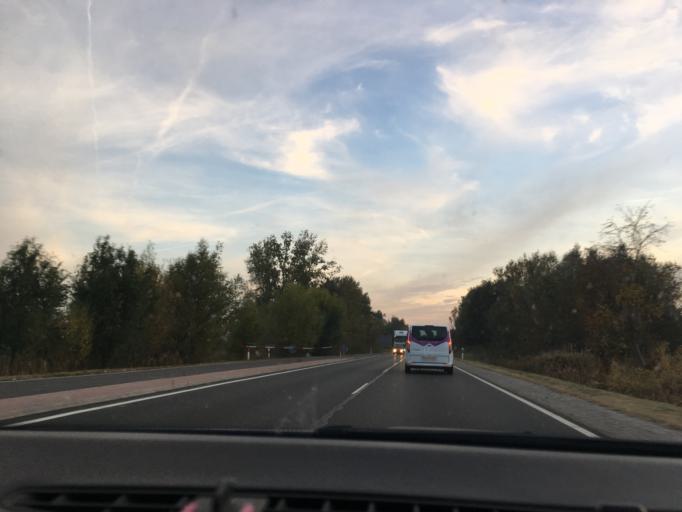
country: HU
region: Hajdu-Bihar
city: Hajduhadhaz
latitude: 47.6942
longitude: 21.6559
